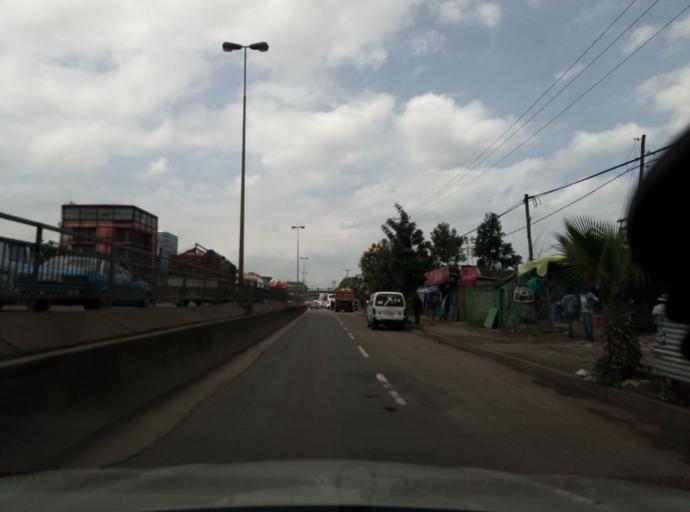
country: ET
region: Adis Abeba
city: Addis Ababa
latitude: 9.0019
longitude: 38.7188
